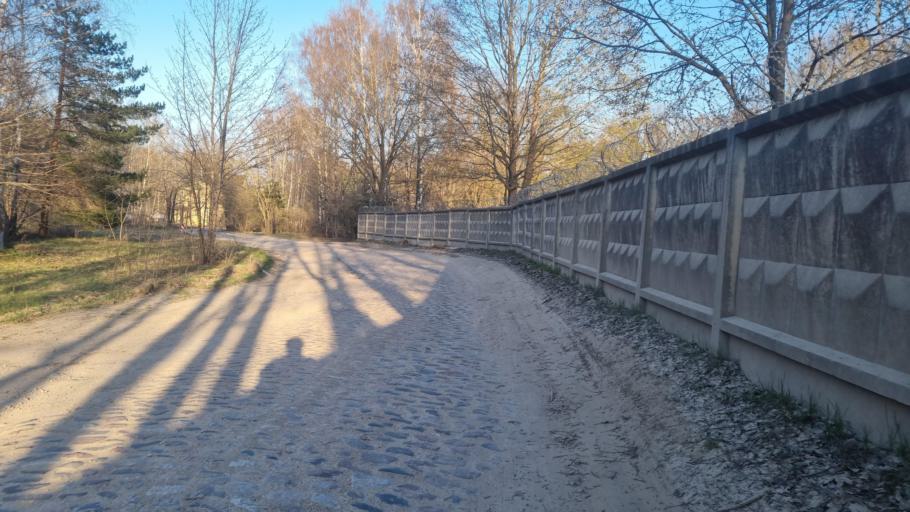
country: LV
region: Kekava
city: Balozi
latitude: 56.9089
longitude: 24.1189
